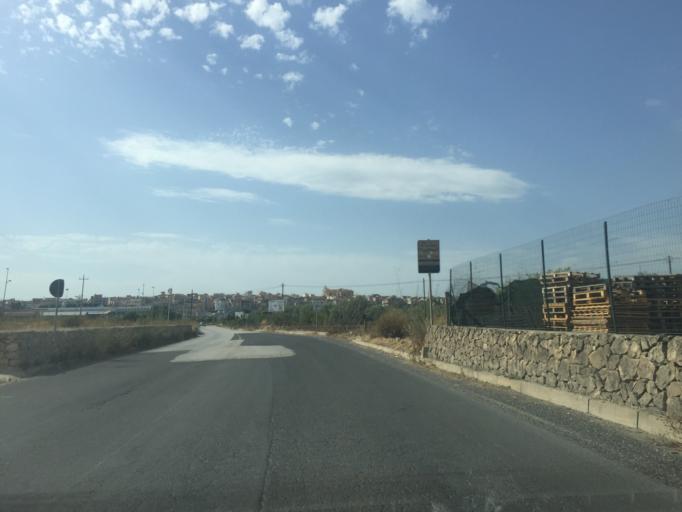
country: IT
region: Sicily
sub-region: Provincia di Siracusa
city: Rosolini
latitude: 36.8134
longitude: 14.9583
